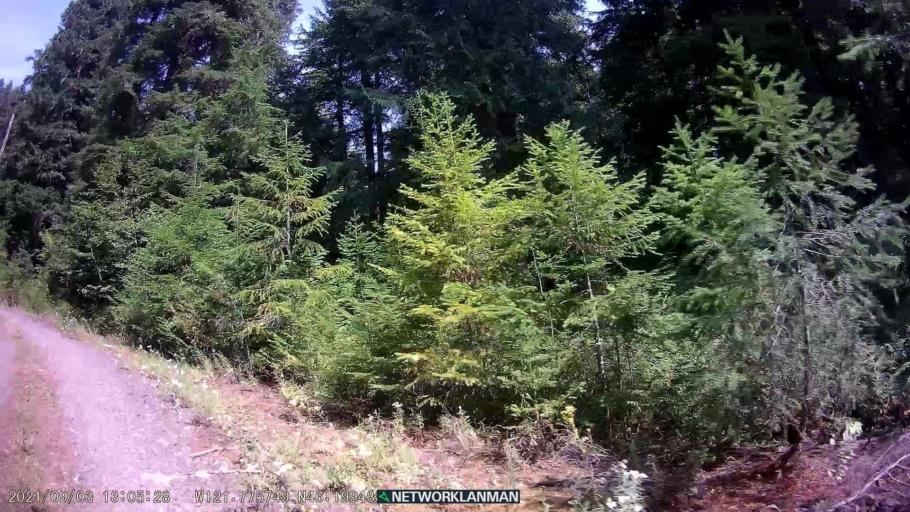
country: US
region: Washington
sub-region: Skamania County
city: Carson
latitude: 46.1985
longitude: -121.7743
